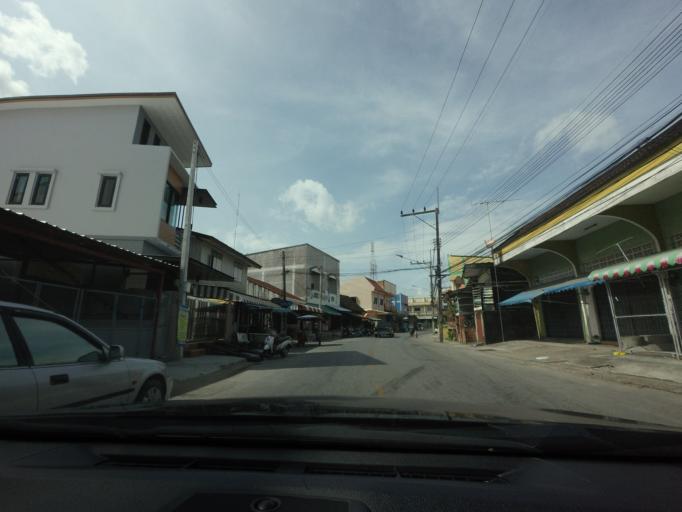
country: TH
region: Pattani
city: Pattani
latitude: 6.8623
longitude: 101.2523
